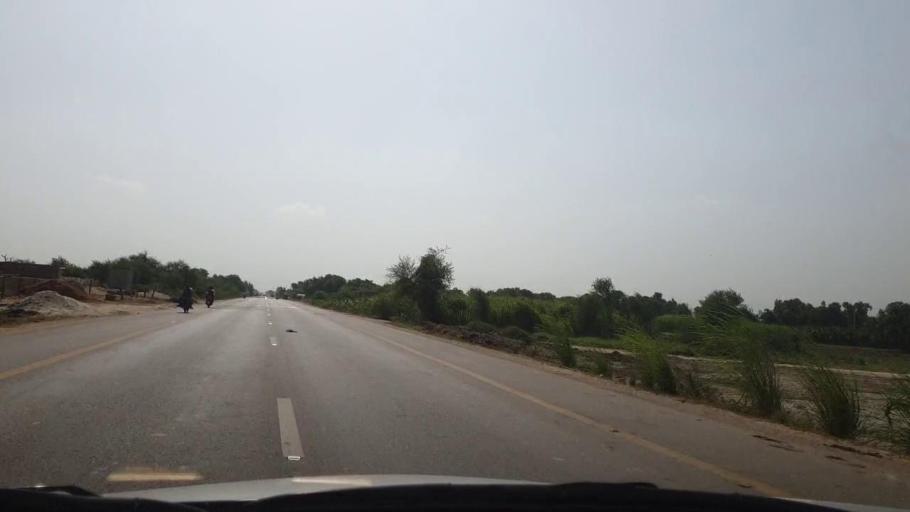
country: PK
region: Sindh
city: Matli
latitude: 25.0667
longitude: 68.6284
